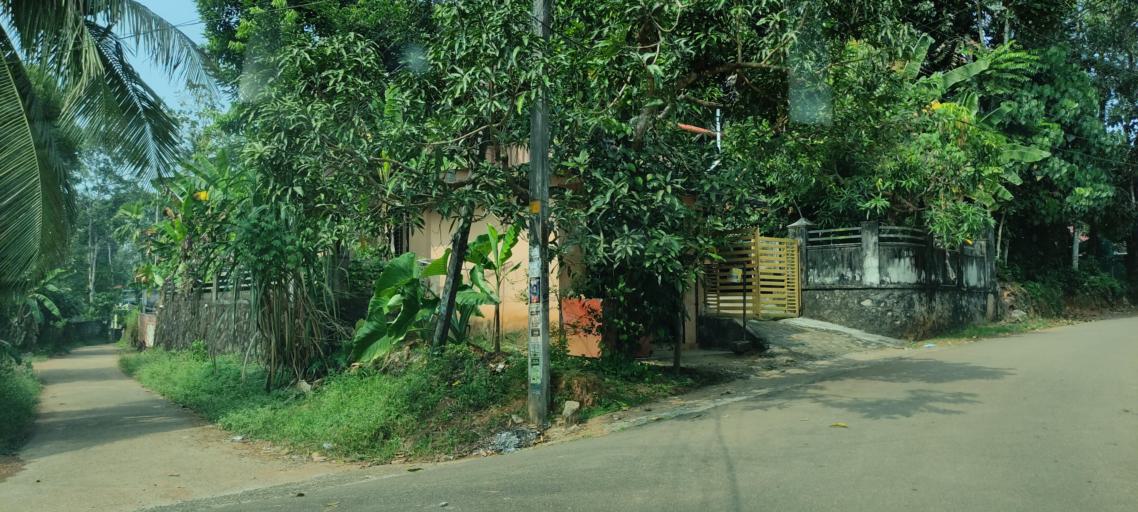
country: IN
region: Kerala
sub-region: Pattanamtitta
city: Adur
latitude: 9.2040
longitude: 76.6925
